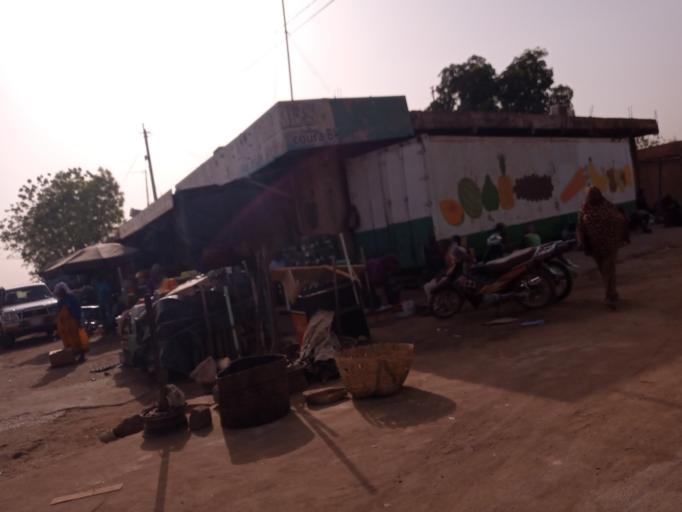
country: ML
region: Bamako
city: Bamako
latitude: 12.6586
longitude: -7.9901
